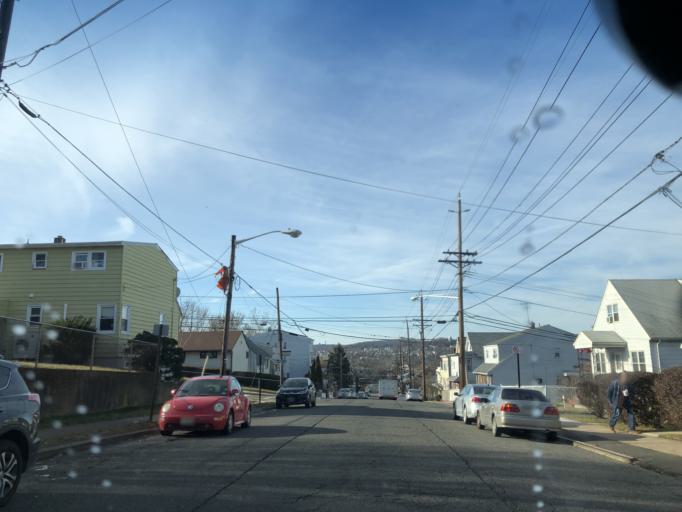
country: US
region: New Jersey
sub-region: Bergen County
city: Fair Lawn
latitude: 40.9351
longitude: -74.1450
